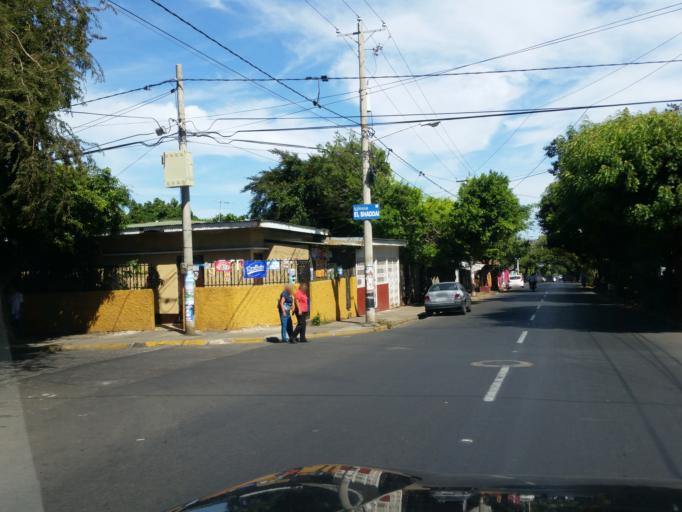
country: NI
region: Managua
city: Managua
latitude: 12.1143
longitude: -86.2968
